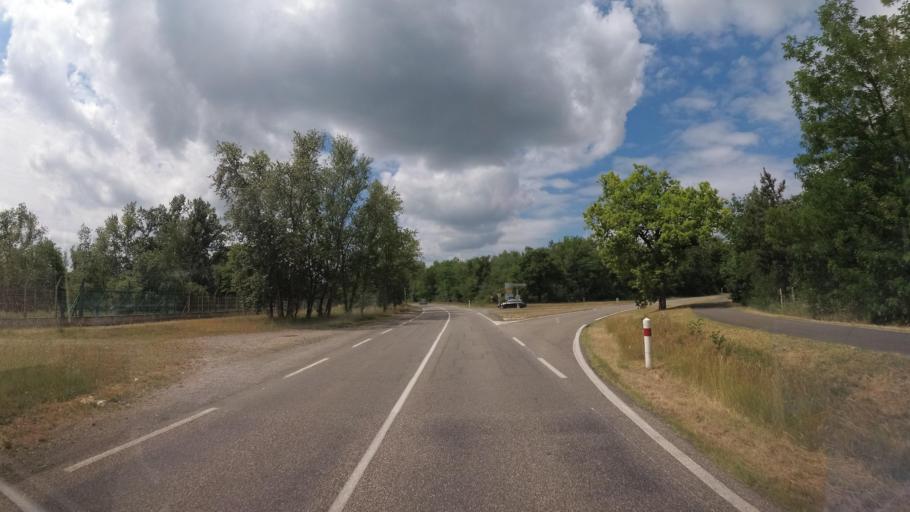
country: FR
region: Alsace
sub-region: Departement du Haut-Rhin
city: Fessenheim
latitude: 47.9122
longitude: 7.5616
